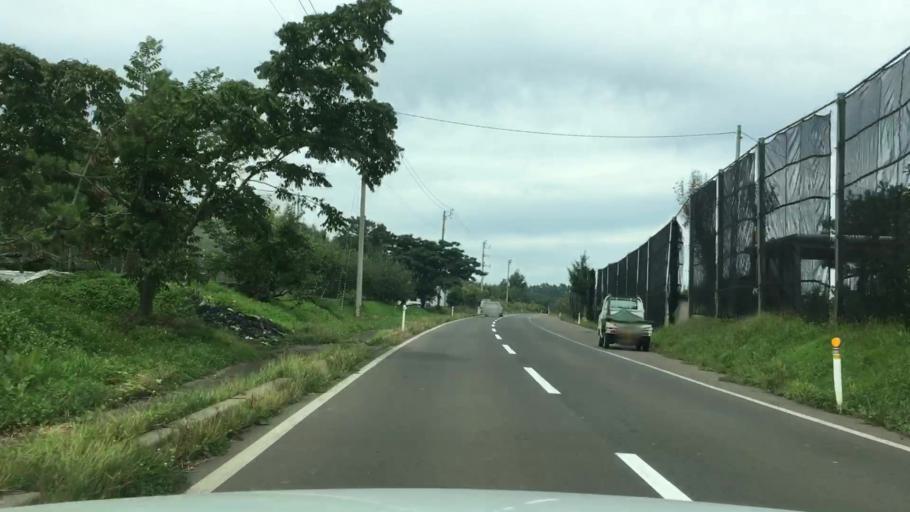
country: JP
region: Aomori
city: Hirosaki
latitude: 40.6714
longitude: 140.3866
